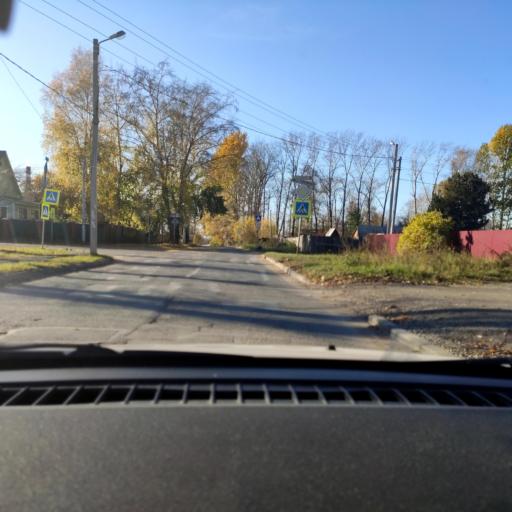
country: RU
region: Perm
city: Perm
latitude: 58.0817
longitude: 56.3598
